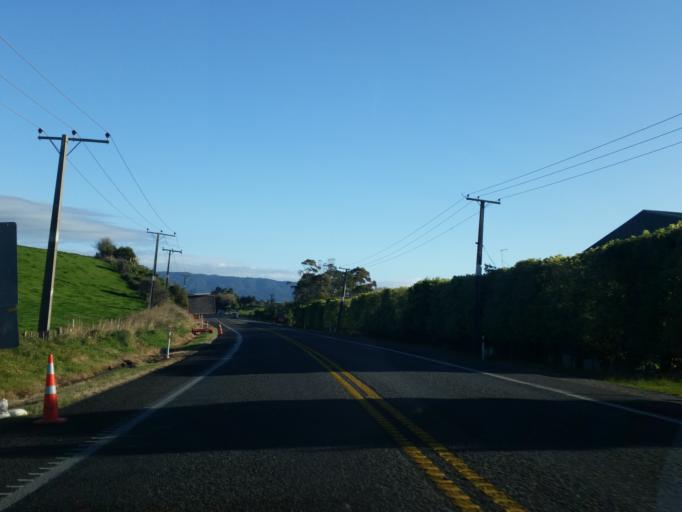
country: NZ
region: Bay of Plenty
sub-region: Western Bay of Plenty District
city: Katikati
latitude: -37.6092
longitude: 175.9445
